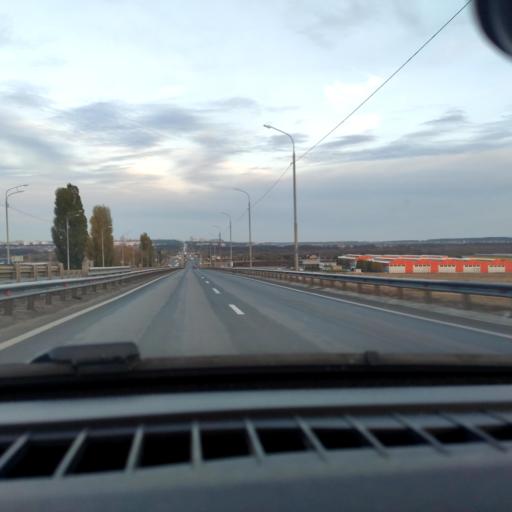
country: RU
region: Voronezj
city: Pridonskoy
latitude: 51.6517
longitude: 39.0530
